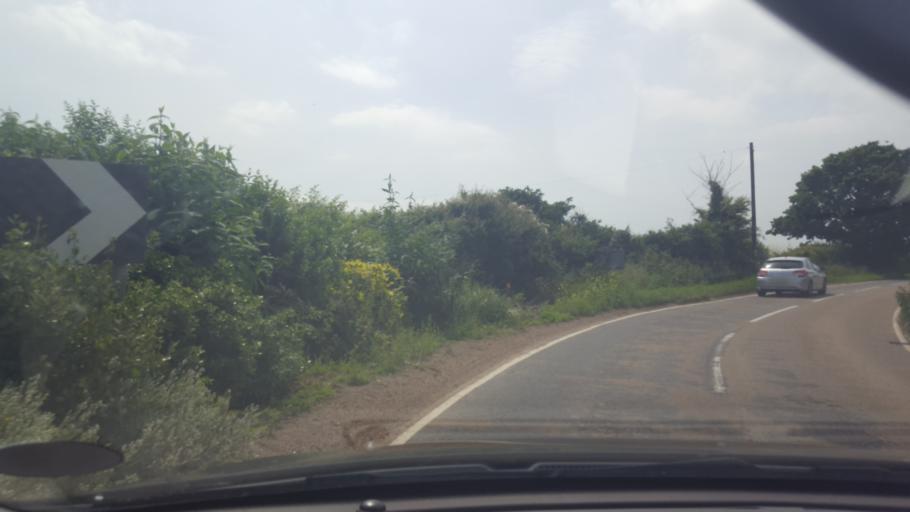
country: GB
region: England
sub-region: Essex
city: Clacton-on-Sea
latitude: 51.8159
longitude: 1.1884
